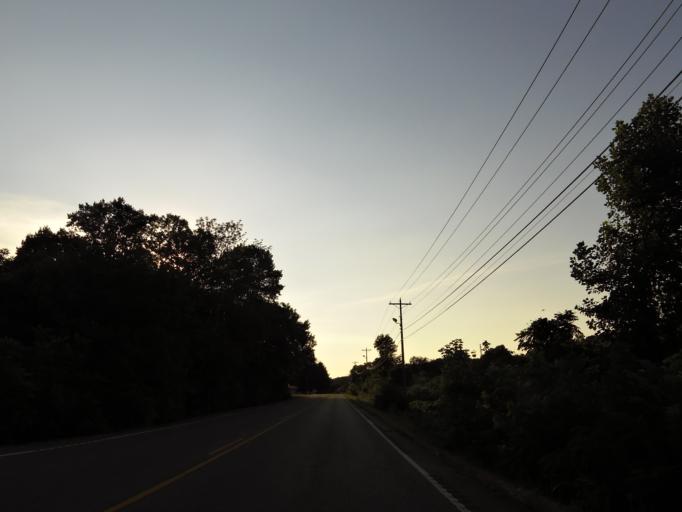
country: US
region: Tennessee
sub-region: McMinn County
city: Athens
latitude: 35.4292
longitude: -84.5735
